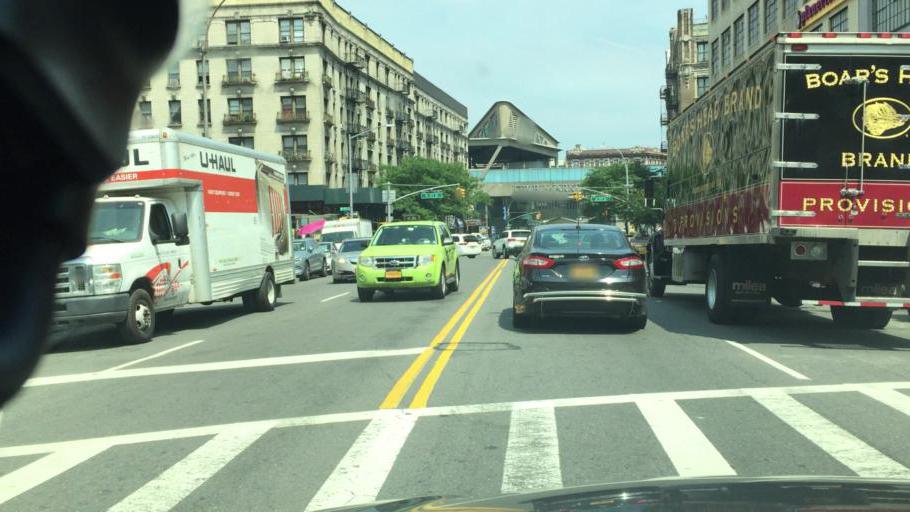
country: US
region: New York
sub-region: New York County
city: Inwood
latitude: 40.8470
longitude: -73.9382
